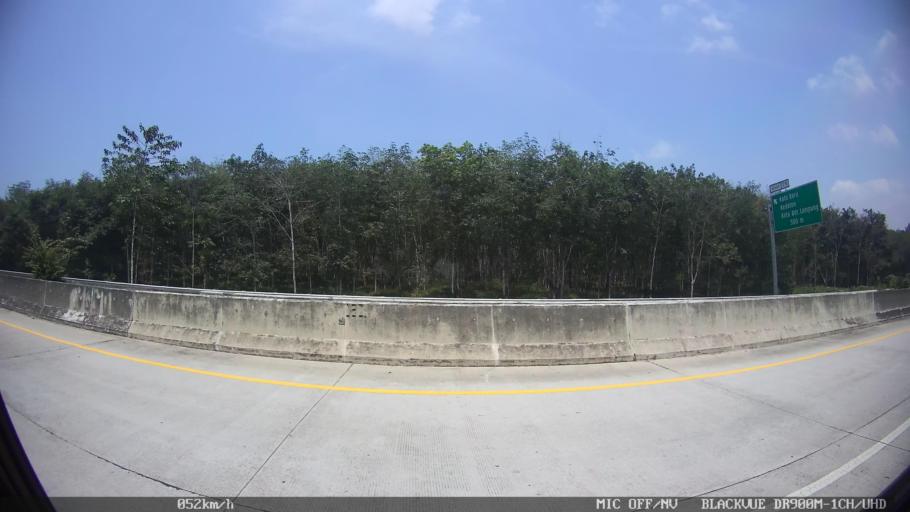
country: ID
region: Lampung
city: Kedaton
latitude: -5.3715
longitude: 105.3270
